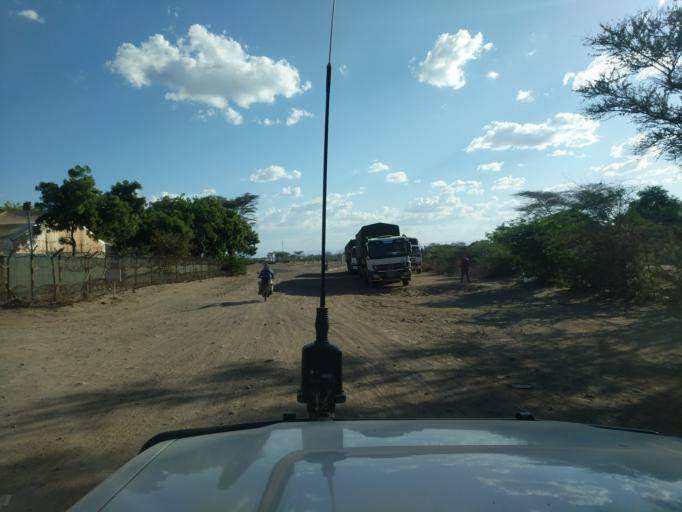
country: UG
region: Northern Region
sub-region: Kaabong District
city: Kaabong
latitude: 3.7144
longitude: 34.8567
